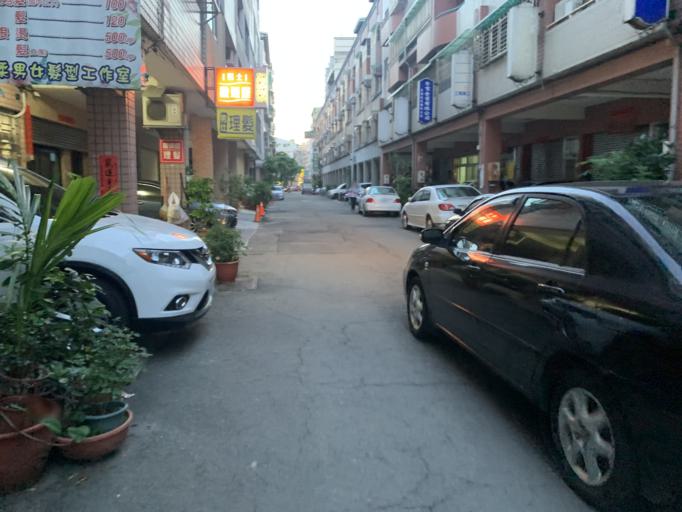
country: TW
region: Taiwan
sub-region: Taichung City
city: Taichung
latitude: 24.1514
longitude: 120.6144
